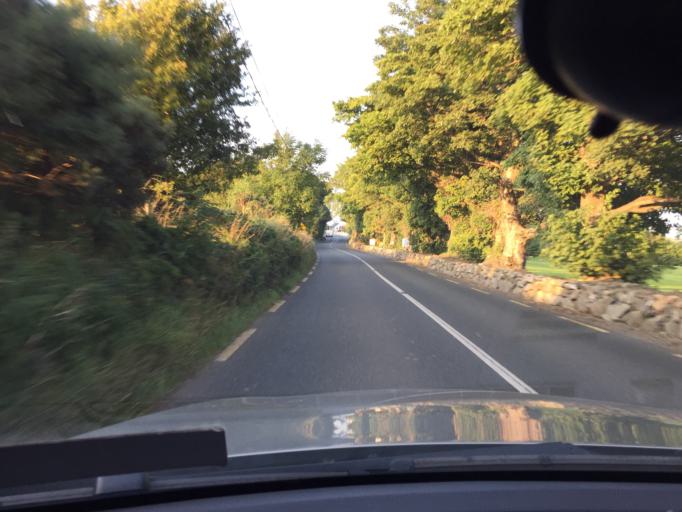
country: IE
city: Newtownmountkennedy
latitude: 53.1031
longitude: -6.1967
